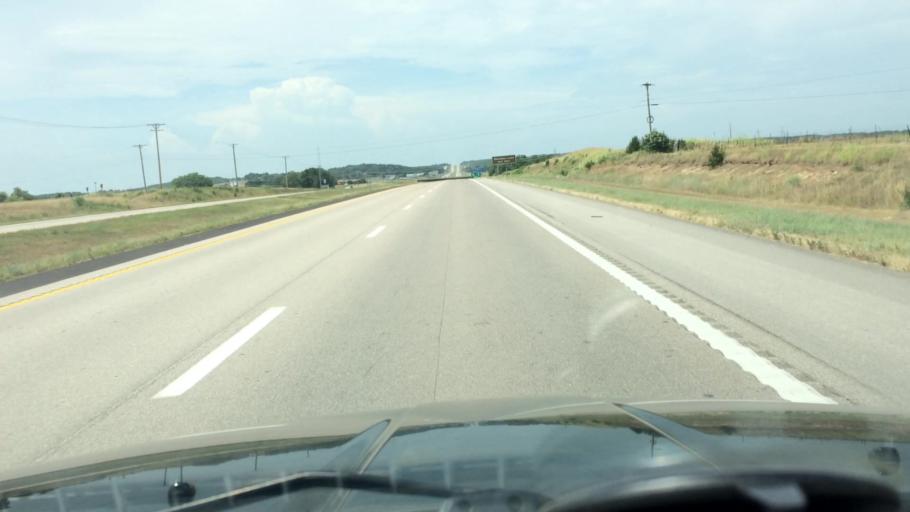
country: US
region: Missouri
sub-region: Polk County
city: Bolivar
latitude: 37.6044
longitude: -93.4409
